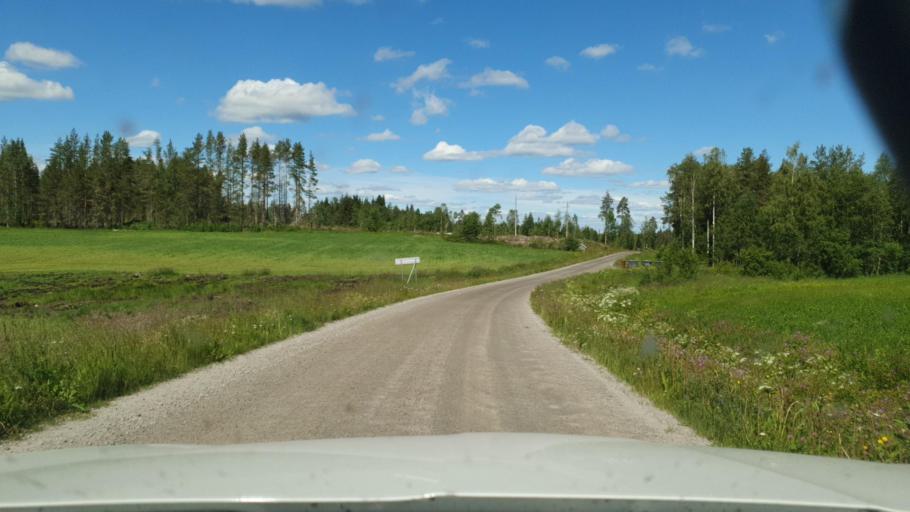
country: SE
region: Vaesterbotten
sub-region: Skelleftea Kommun
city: Byske
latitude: 65.1234
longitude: 21.2050
